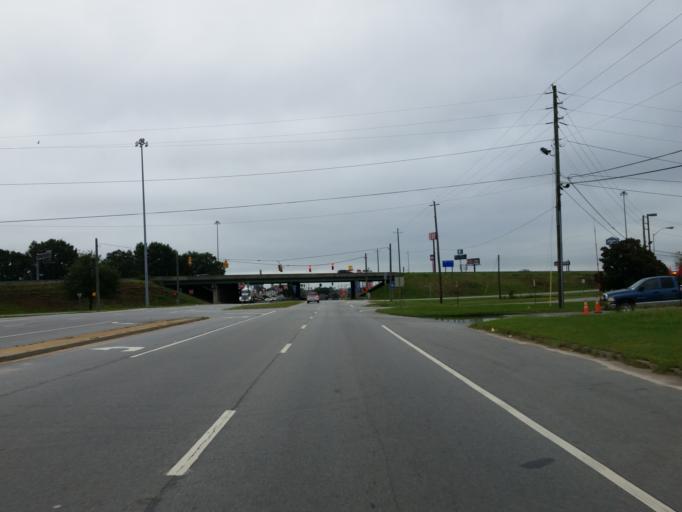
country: US
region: Georgia
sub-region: Houston County
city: Perry
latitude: 32.4729
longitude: -83.7454
